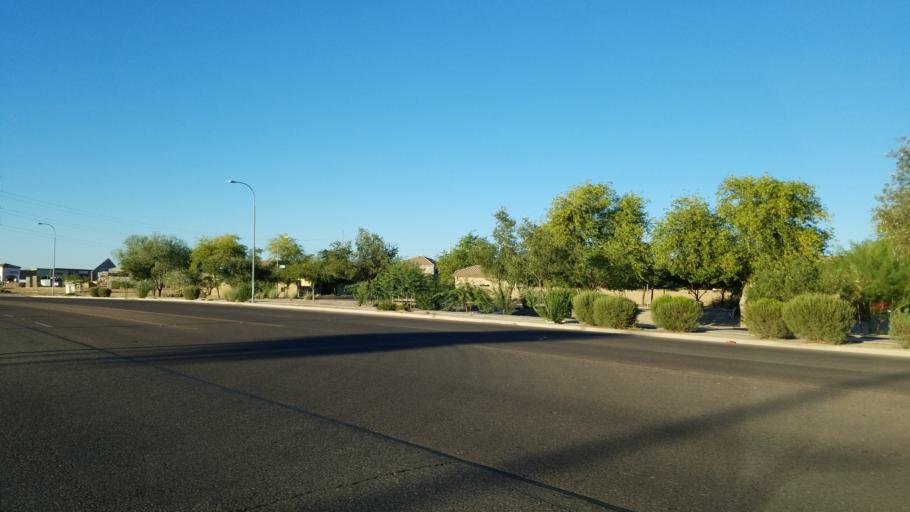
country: US
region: Arizona
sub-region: Maricopa County
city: Laveen
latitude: 33.3754
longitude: -112.1171
